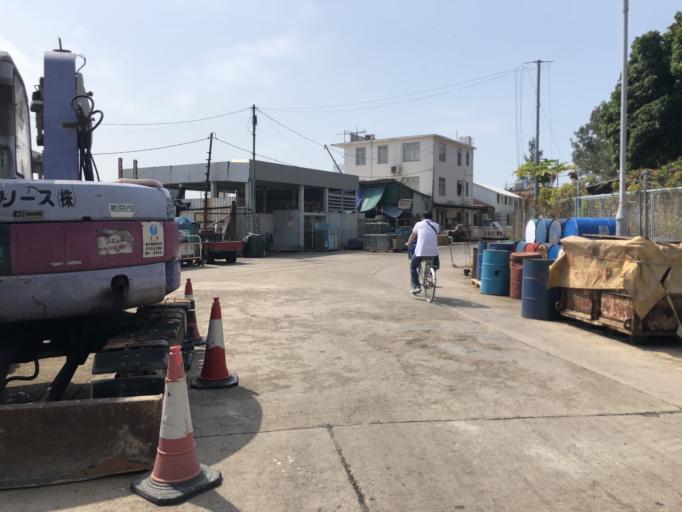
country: HK
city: Yung Shue Wan
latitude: 22.2121
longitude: 114.0251
